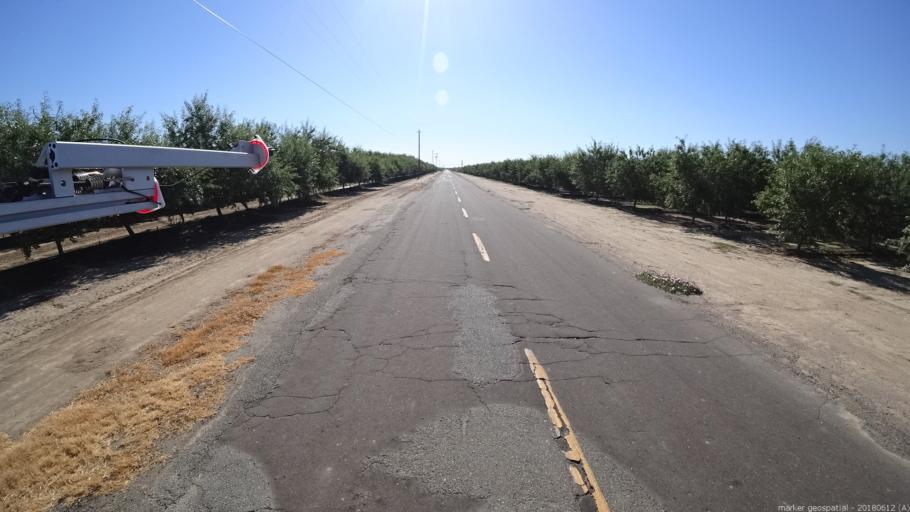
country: US
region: California
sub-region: Madera County
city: Fairmead
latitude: 37.0111
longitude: -120.2731
